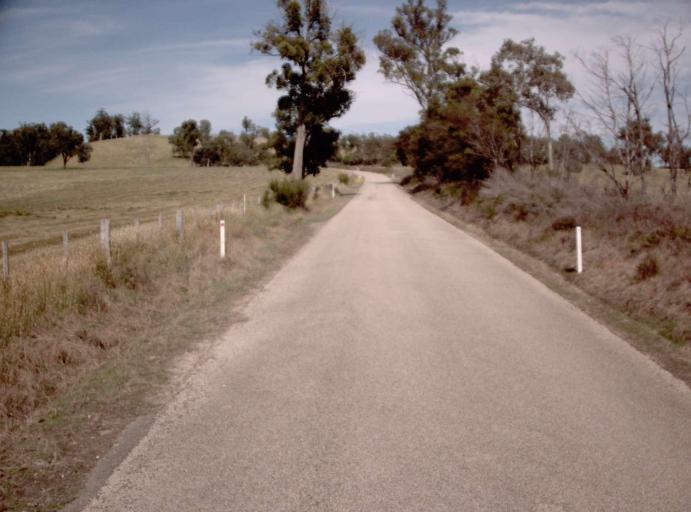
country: AU
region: Victoria
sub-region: East Gippsland
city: Lakes Entrance
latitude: -37.5239
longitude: 148.1484
